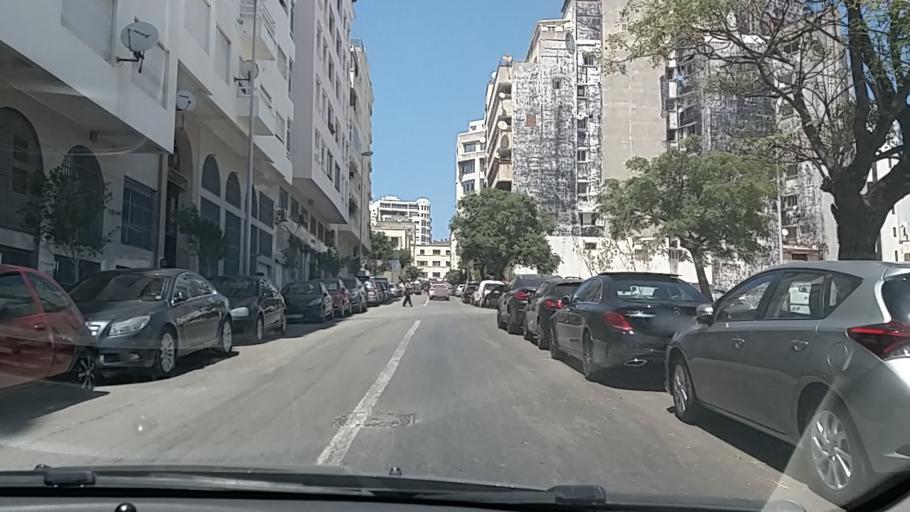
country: MA
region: Tanger-Tetouan
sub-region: Tanger-Assilah
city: Tangier
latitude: 35.7764
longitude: -5.8079
